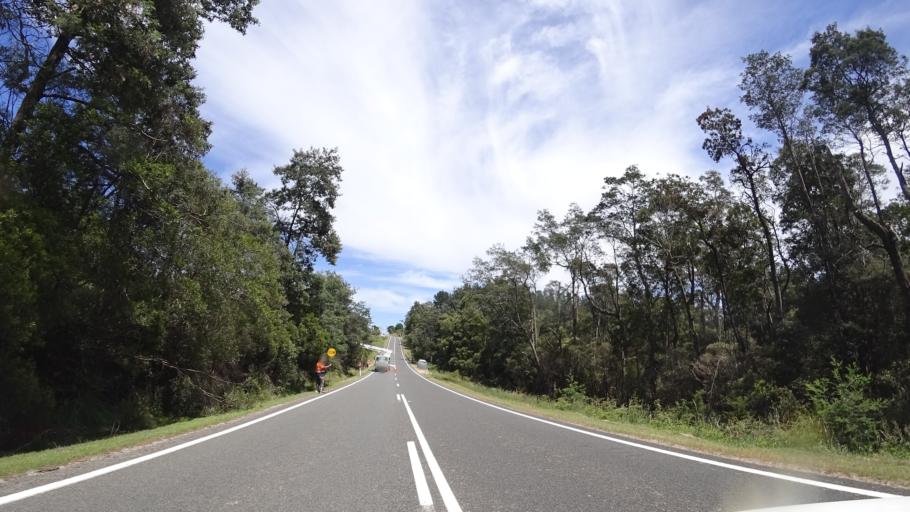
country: AU
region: Tasmania
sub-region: Dorset
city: Scottsdale
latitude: -41.1680
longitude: 147.7542
